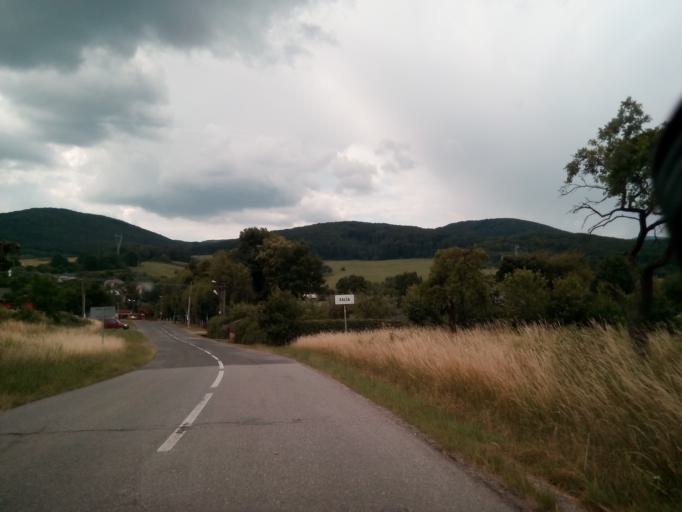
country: SK
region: Kosicky
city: Secovce
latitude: 48.6164
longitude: 21.5224
